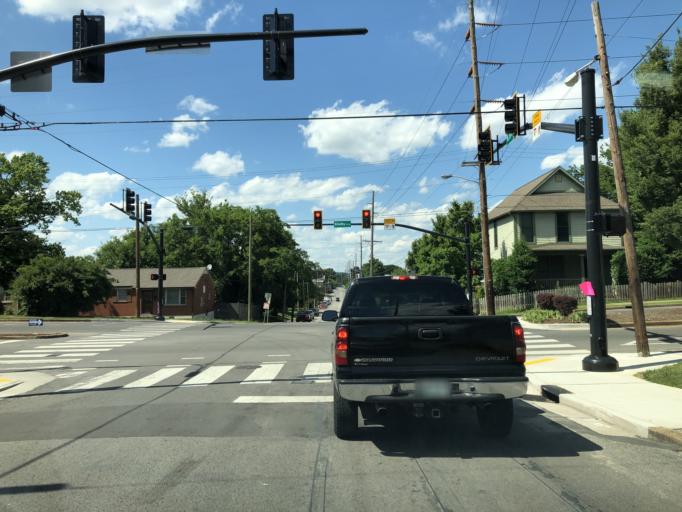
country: US
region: Tennessee
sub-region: Davidson County
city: Nashville
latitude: 36.1710
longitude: -86.7508
